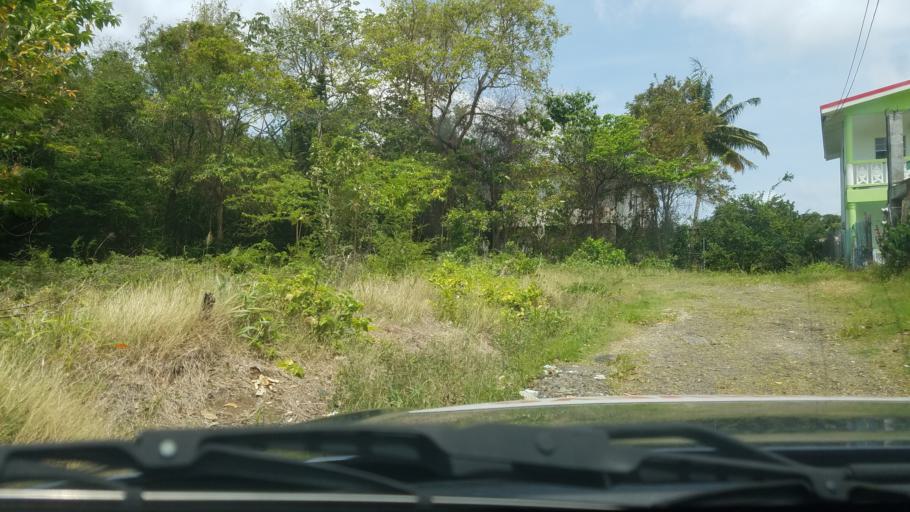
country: LC
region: Castries Quarter
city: Bisee
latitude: 14.0423
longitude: -60.9607
